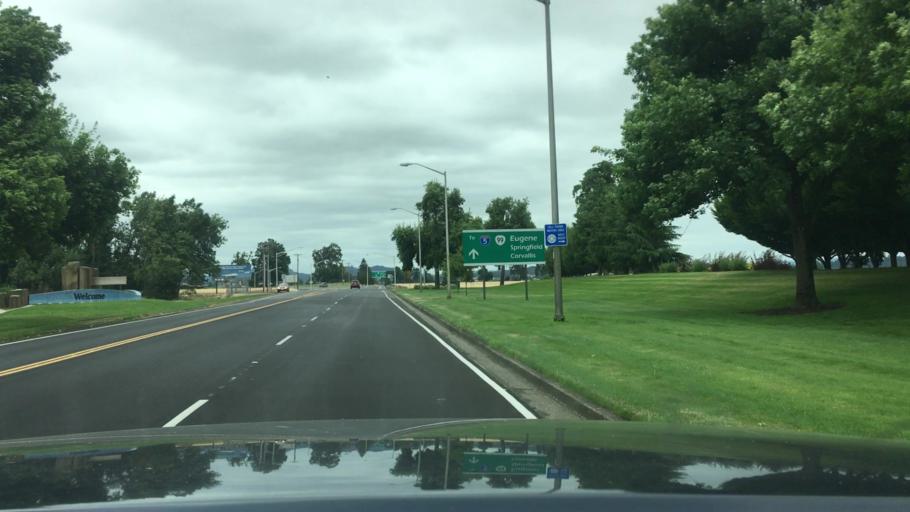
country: US
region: Oregon
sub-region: Lane County
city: Junction City
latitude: 44.1150
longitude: -123.2085
